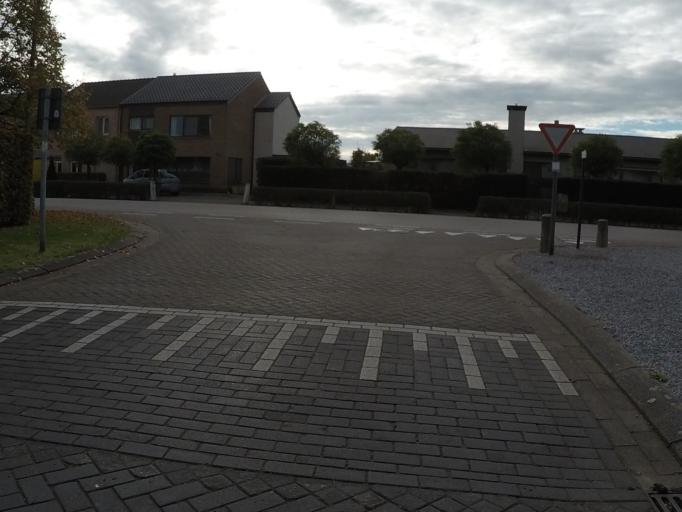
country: BE
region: Flanders
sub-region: Provincie Antwerpen
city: Nijlen
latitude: 51.1388
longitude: 4.6783
